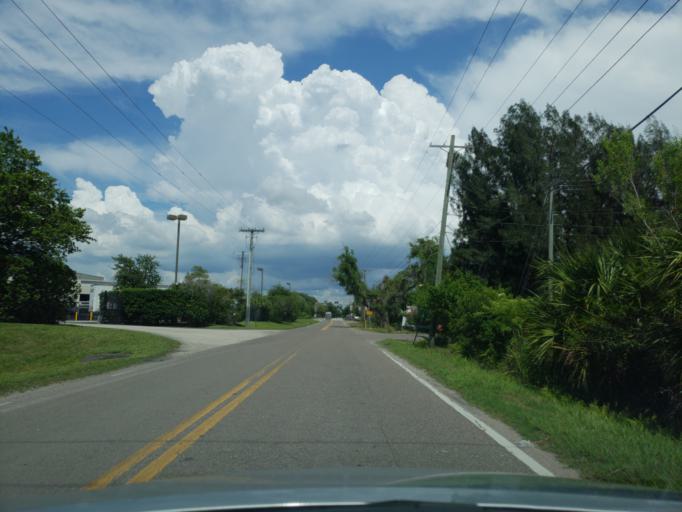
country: US
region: Florida
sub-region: Hillsborough County
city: Palm River-Clair Mel
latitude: 27.9336
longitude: -82.3996
